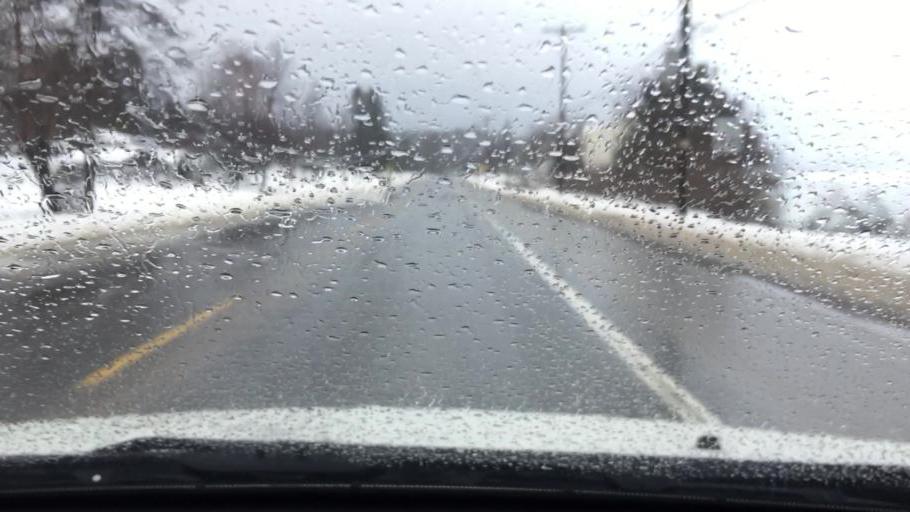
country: US
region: Michigan
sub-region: Charlevoix County
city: East Jordan
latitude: 45.1575
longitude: -85.1447
